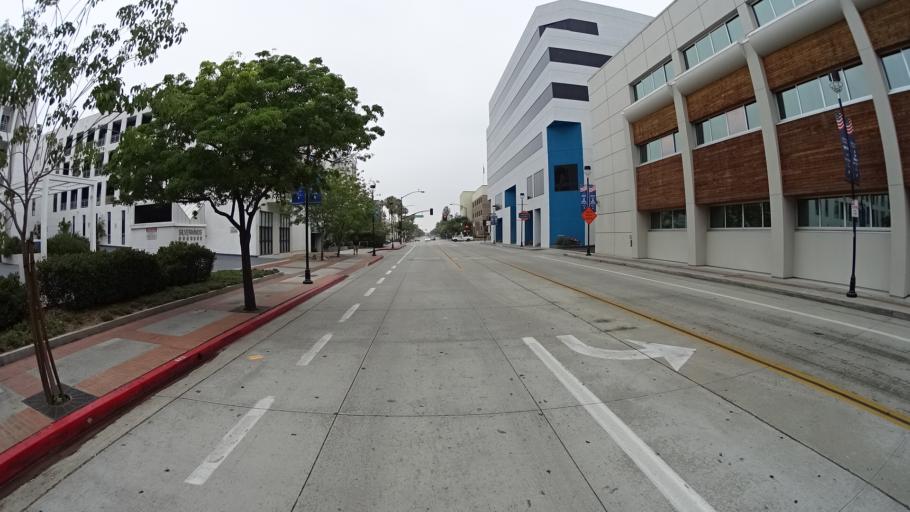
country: US
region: California
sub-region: Los Angeles County
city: Burbank
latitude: 34.1837
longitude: -118.3098
